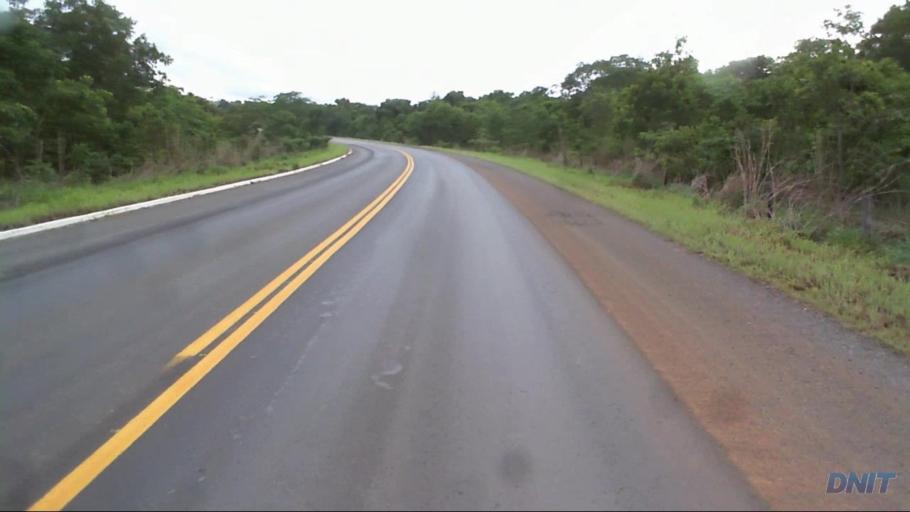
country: BR
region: Goias
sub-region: Padre Bernardo
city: Padre Bernardo
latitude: -15.2200
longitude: -48.5500
